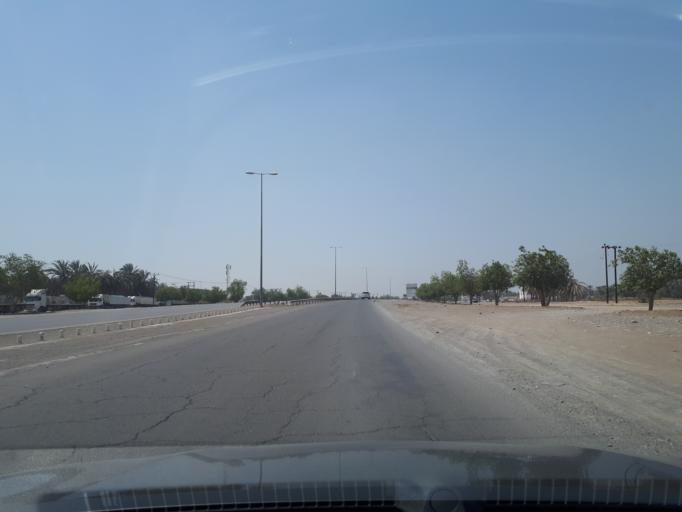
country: OM
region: Al Batinah
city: Al Liwa'
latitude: 24.5088
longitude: 56.5637
